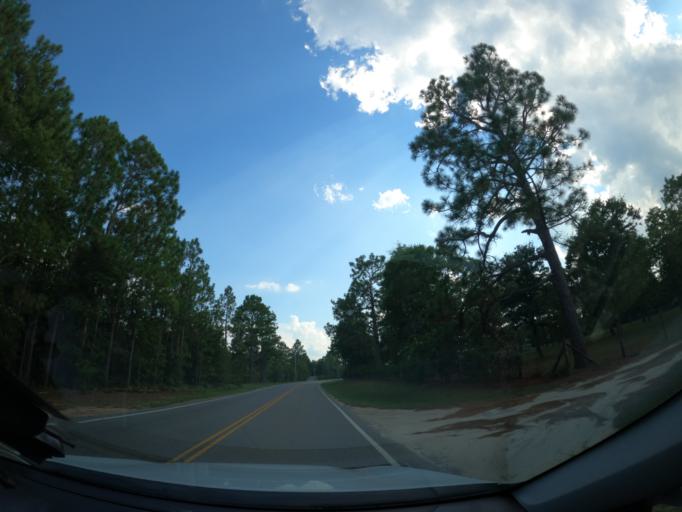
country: US
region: South Carolina
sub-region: Barnwell County
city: Williston
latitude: 33.5097
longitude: -81.5052
